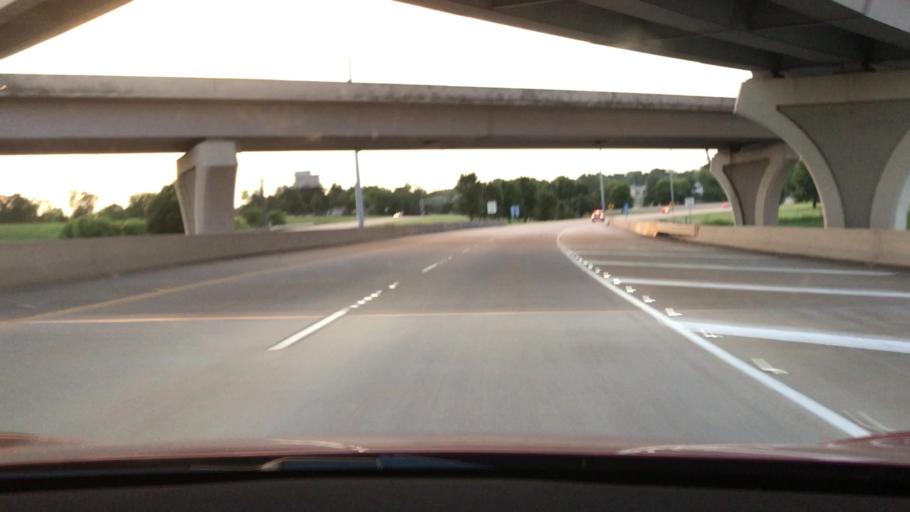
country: US
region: Louisiana
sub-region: Caddo Parish
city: Shreveport
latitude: 32.4963
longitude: -93.7594
